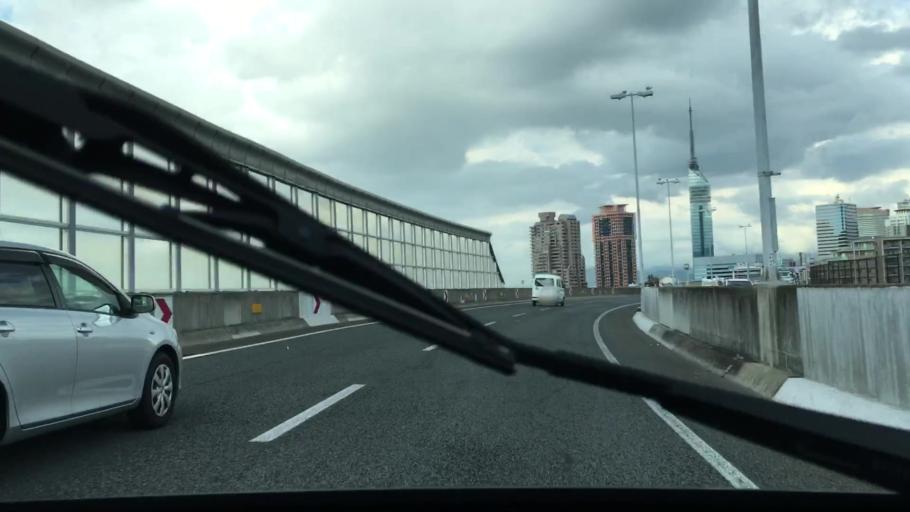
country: JP
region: Fukuoka
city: Fukuoka-shi
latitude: 33.5877
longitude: 130.3417
